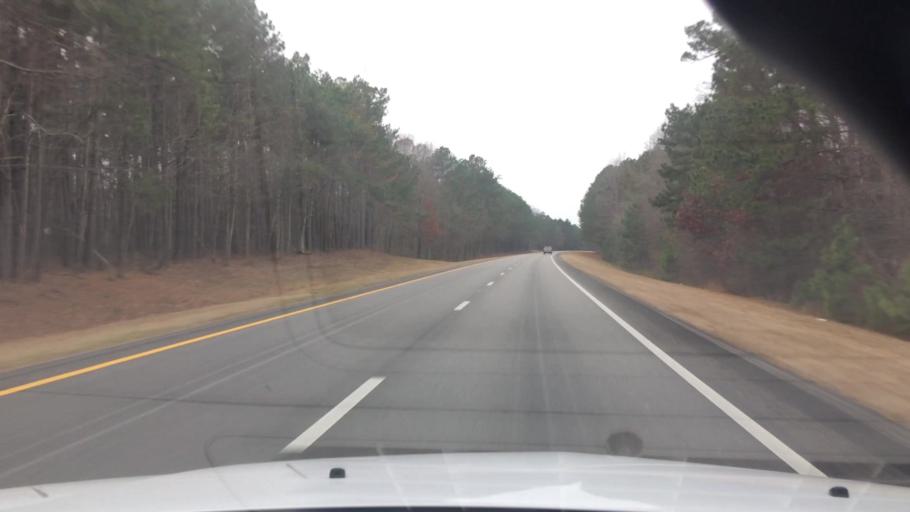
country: US
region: North Carolina
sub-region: Nash County
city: Spring Hope
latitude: 35.9321
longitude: -78.0757
